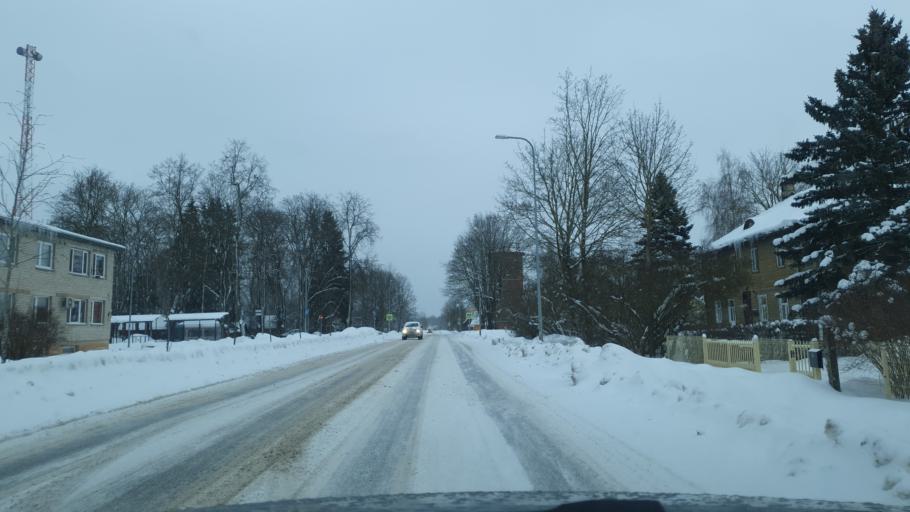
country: EE
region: Polvamaa
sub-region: Polva linn
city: Polva
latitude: 58.0697
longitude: 27.0892
